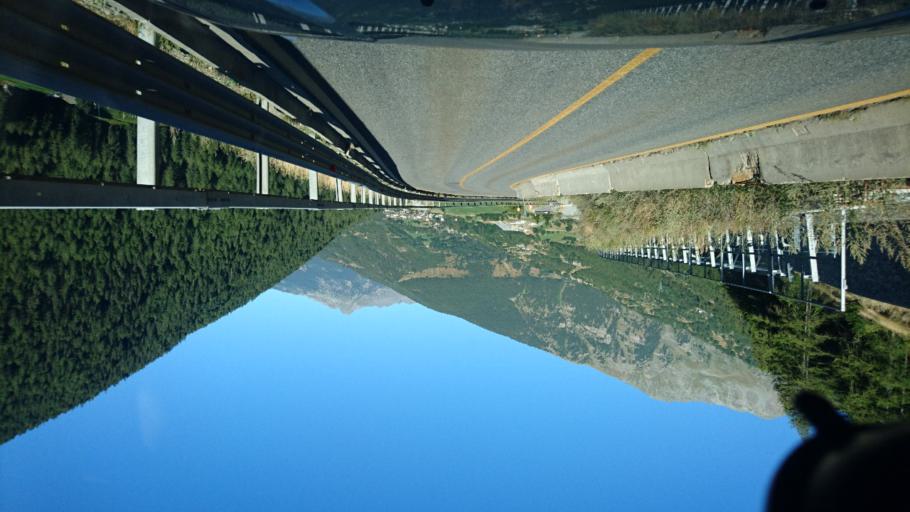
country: IT
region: Aosta Valley
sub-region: Valle d'Aosta
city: Saint-Oyen
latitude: 45.8227
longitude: 7.2014
